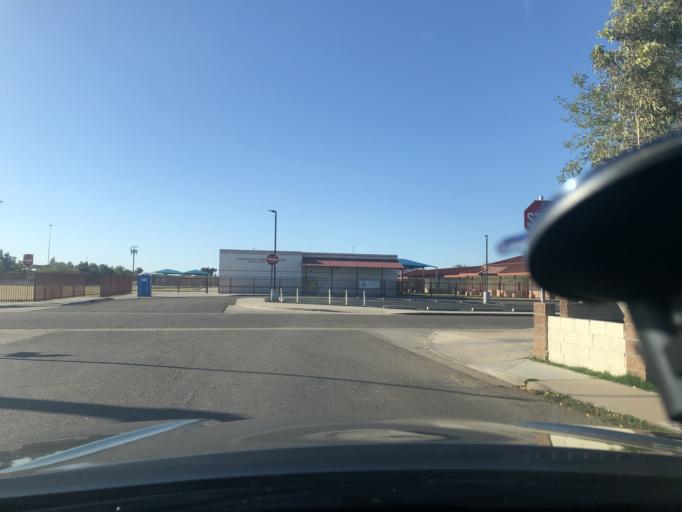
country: US
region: Arizona
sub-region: Maricopa County
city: Phoenix
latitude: 33.4640
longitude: -112.0334
